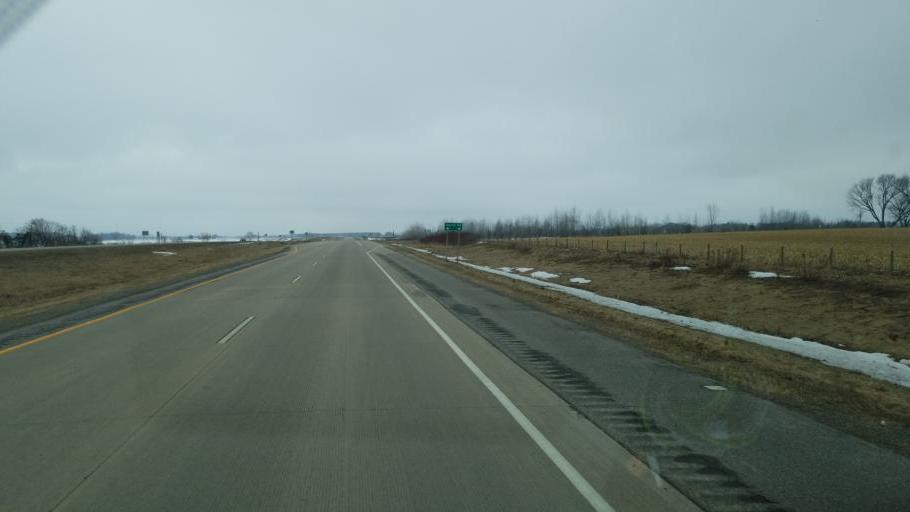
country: US
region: Wisconsin
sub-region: Wood County
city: Marshfield
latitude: 44.6201
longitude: -90.0016
